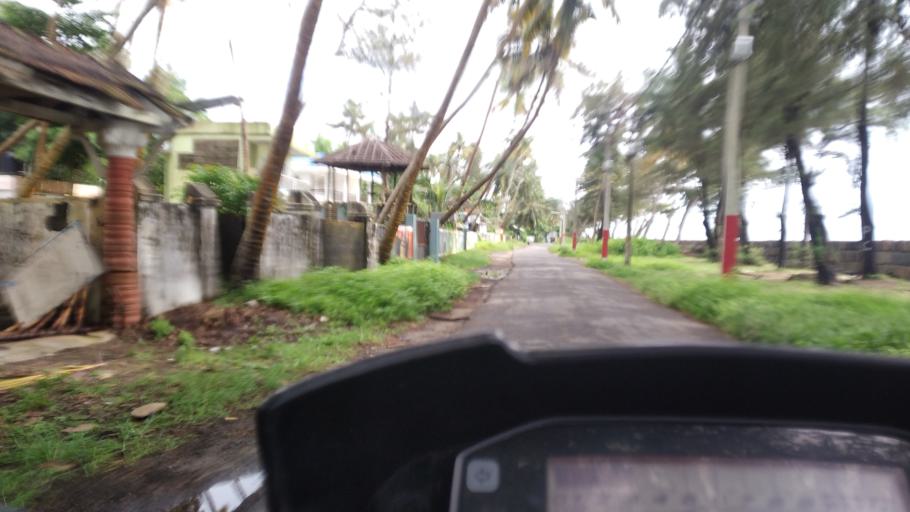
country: IN
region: Kerala
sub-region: Thrissur District
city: Kodungallur
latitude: 10.1586
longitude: 76.1726
